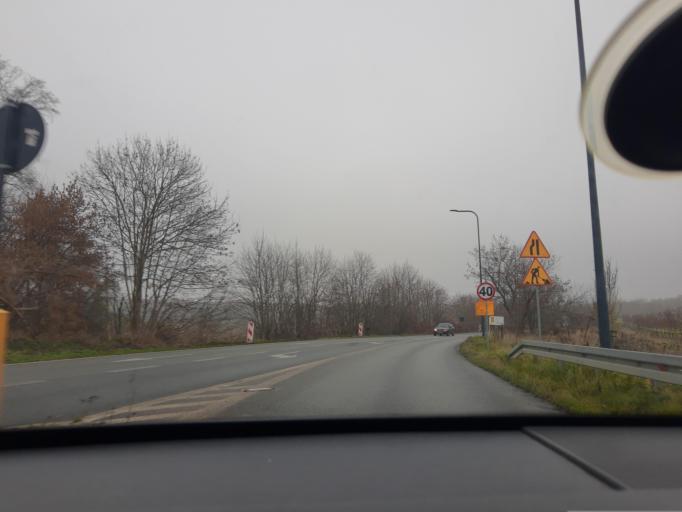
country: PL
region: Lodz Voivodeship
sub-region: Powiat pabianicki
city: Konstantynow Lodzki
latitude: 51.7548
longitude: 19.3866
